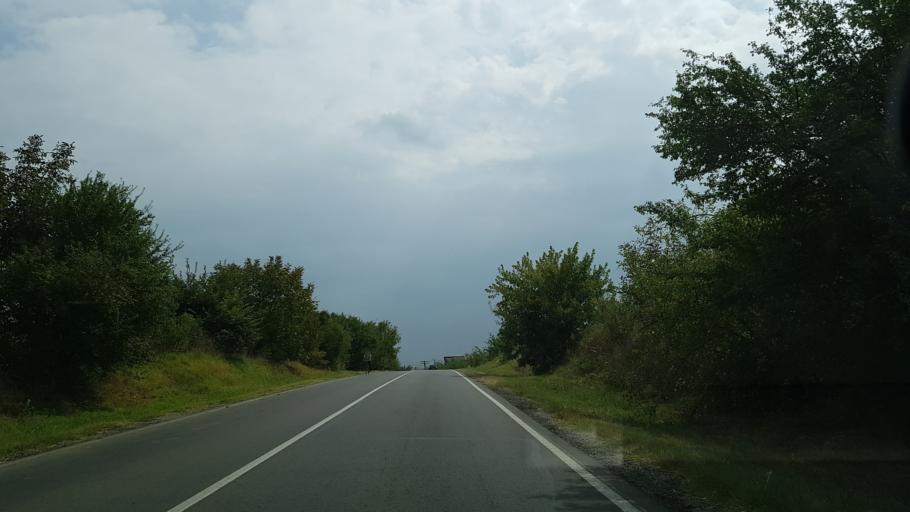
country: RO
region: Ilfov
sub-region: Comuna Ganeasa
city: Piteasca
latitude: 44.4778
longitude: 26.3146
